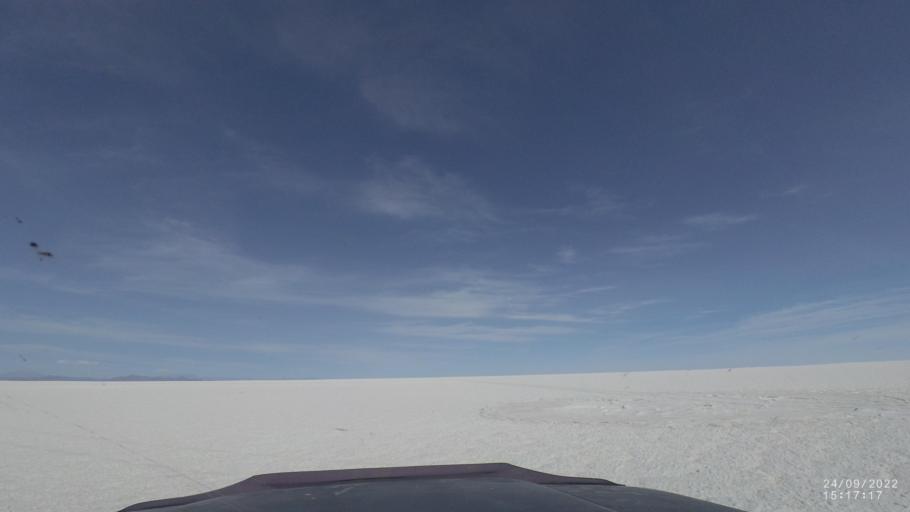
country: BO
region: Potosi
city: Colchani
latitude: -19.9881
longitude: -67.4283
